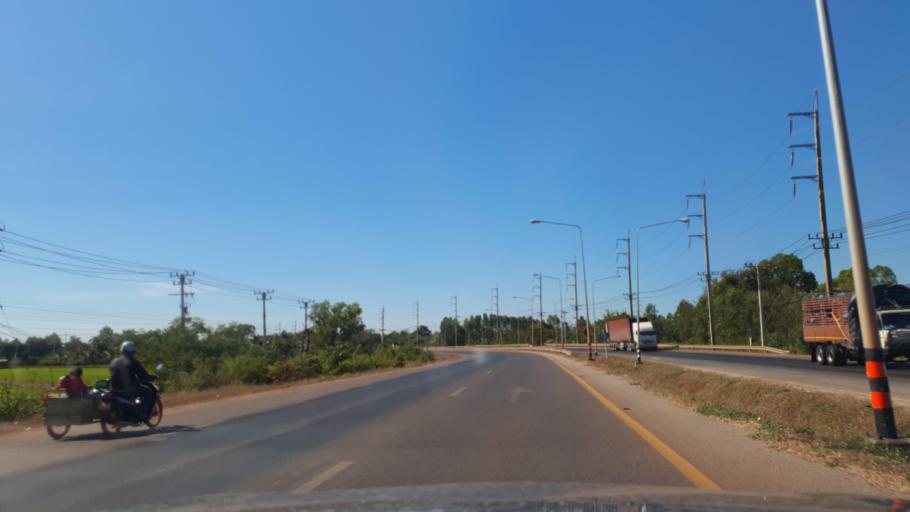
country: TH
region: Sakon Nakhon
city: Sakon Nakhon
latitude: 17.2617
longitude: 104.1189
